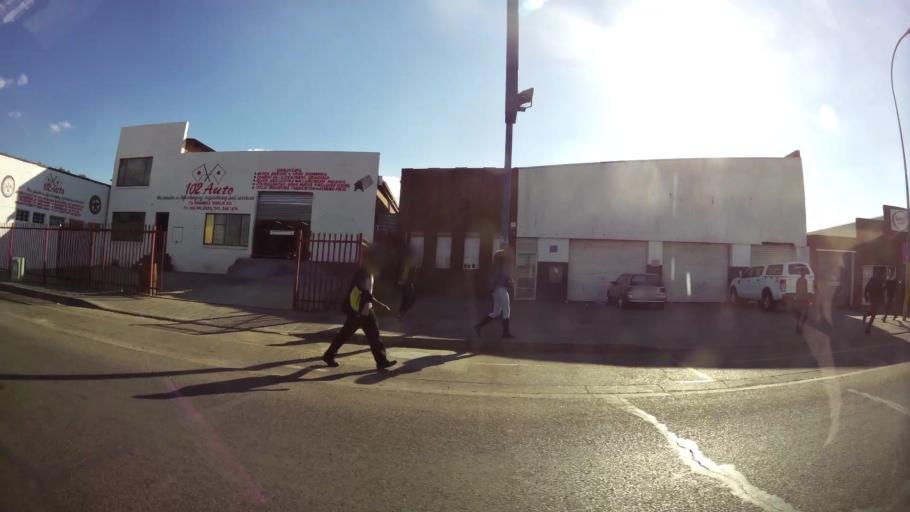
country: ZA
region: Northern Cape
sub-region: Frances Baard District Municipality
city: Kimberley
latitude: -28.7316
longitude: 24.7641
